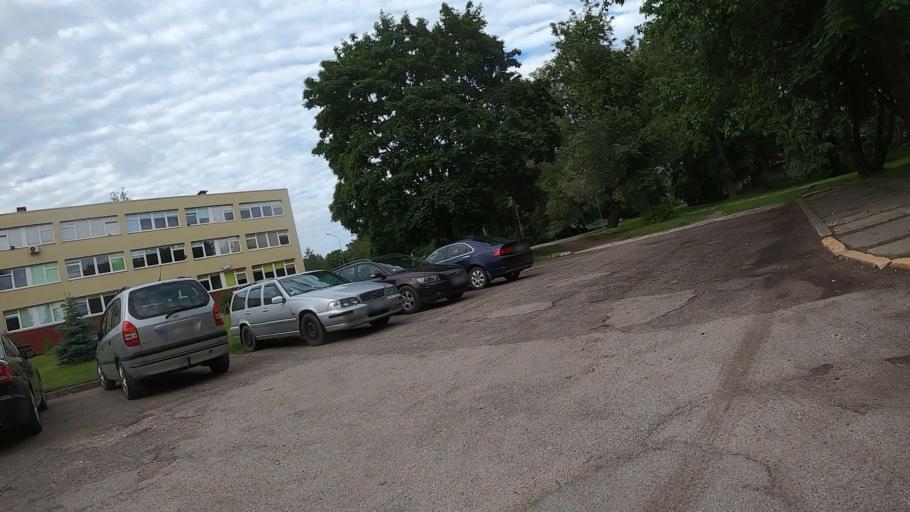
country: LV
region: Ozolnieku
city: Ozolnieki
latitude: 56.6695
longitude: 23.7514
